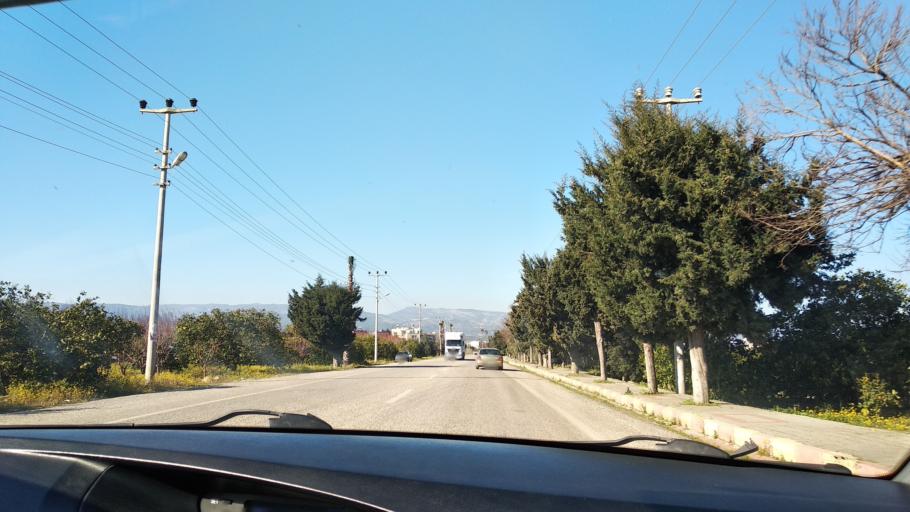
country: TR
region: Mersin
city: Tomuk
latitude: 36.6505
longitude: 34.3695
